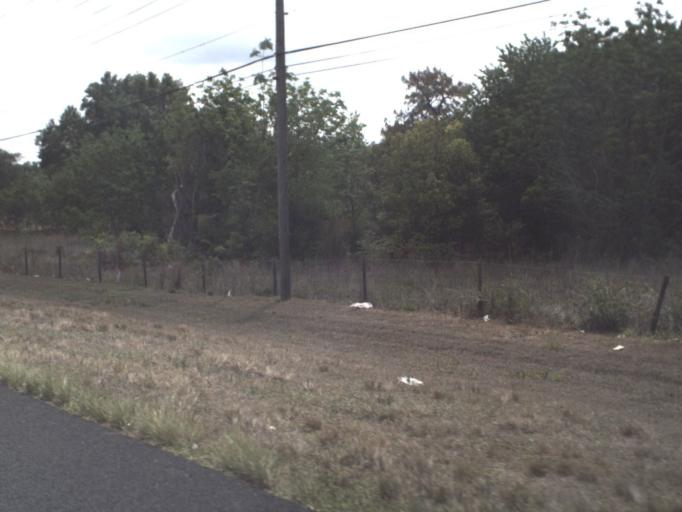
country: US
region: Florida
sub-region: Lake County
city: Groveland
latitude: 28.5579
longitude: -81.8265
